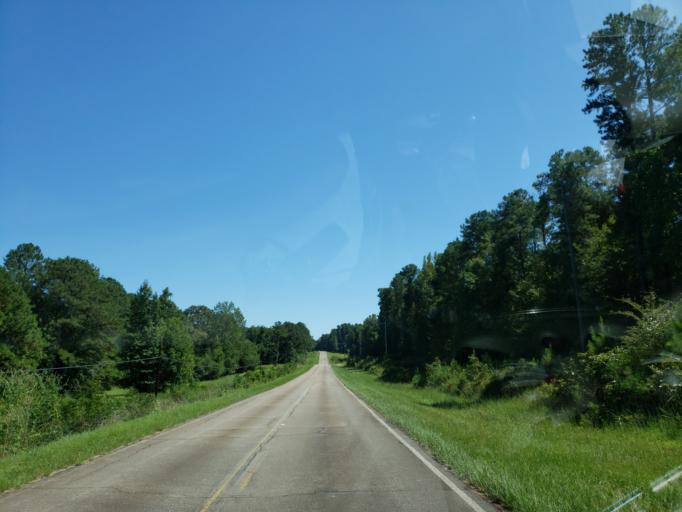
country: US
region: Georgia
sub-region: Crawford County
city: Roberta
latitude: 32.8281
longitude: -84.0713
